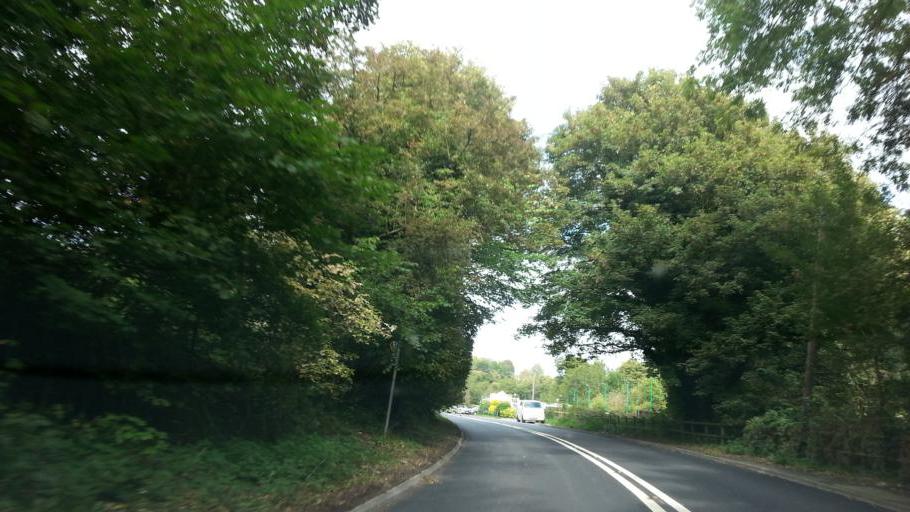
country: GB
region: England
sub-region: Gloucestershire
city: Stroud
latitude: 51.7600
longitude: -2.2223
